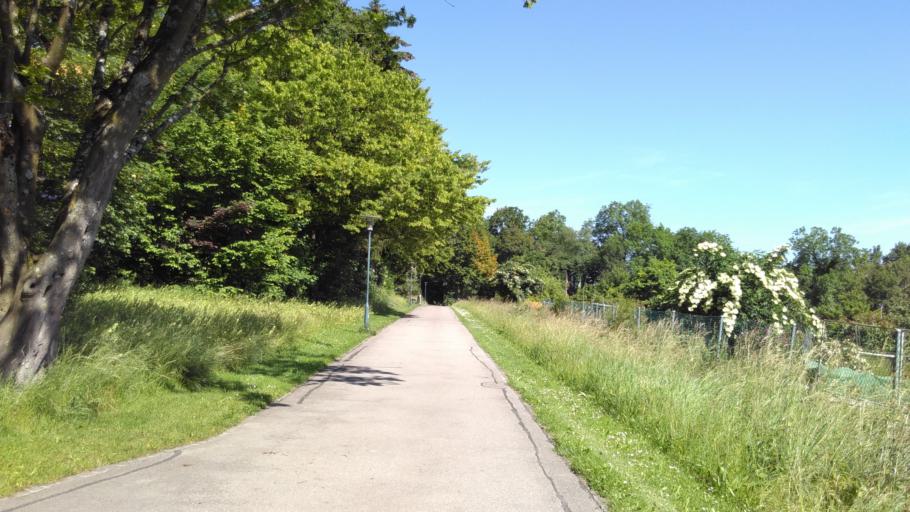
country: CH
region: Zurich
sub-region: Bezirk Zuerich
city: Zuerich (Kreis 3)
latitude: 47.3544
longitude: 8.5049
